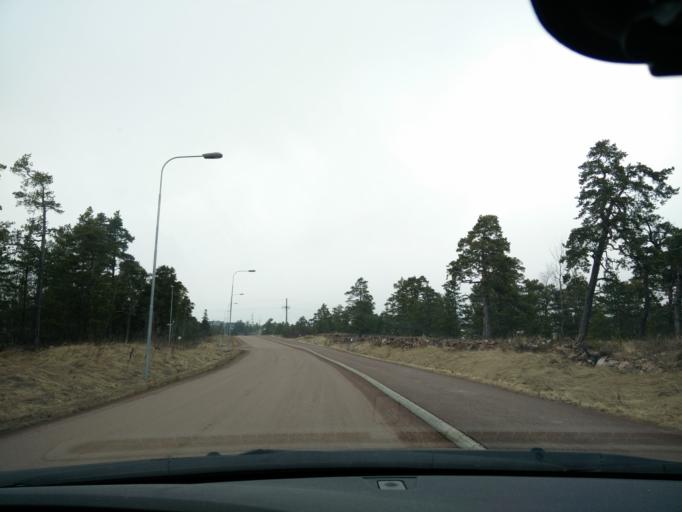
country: AX
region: Mariehamns stad
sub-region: Mariehamn
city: Mariehamn
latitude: 60.1263
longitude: 19.9293
